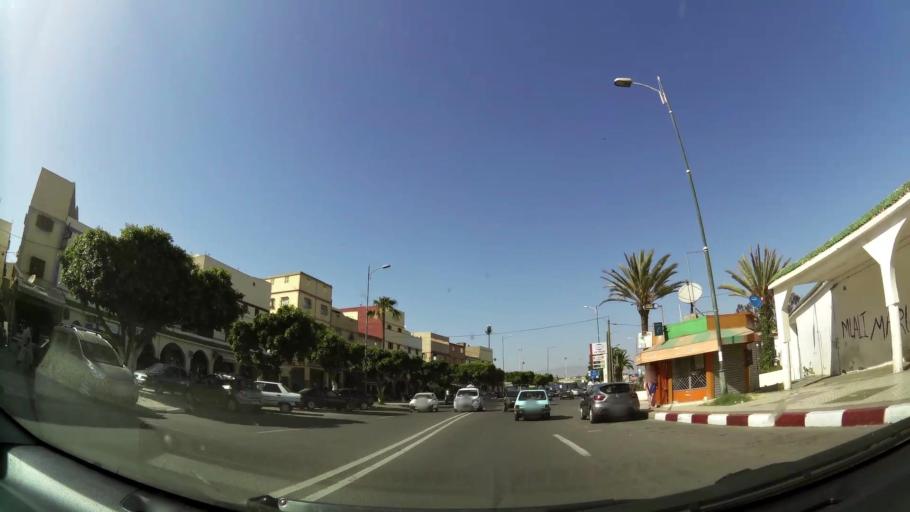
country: MA
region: Souss-Massa-Draa
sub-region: Inezgane-Ait Mellou
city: Inezgane
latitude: 30.3702
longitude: -9.5325
